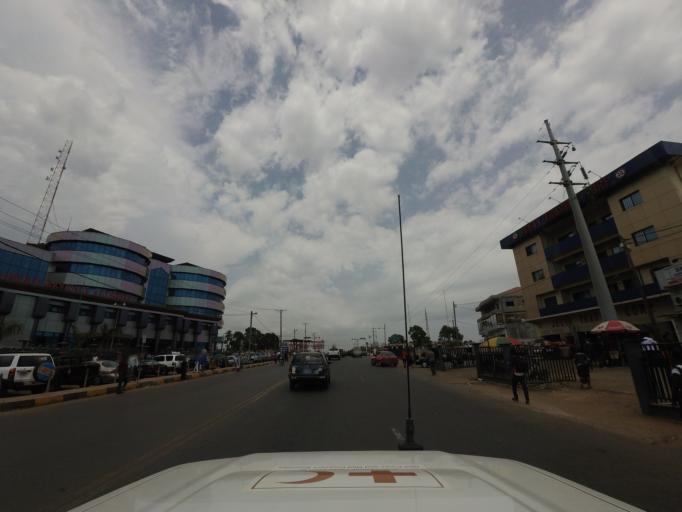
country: LR
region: Montserrado
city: Monrovia
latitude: 6.2646
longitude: -10.7050
